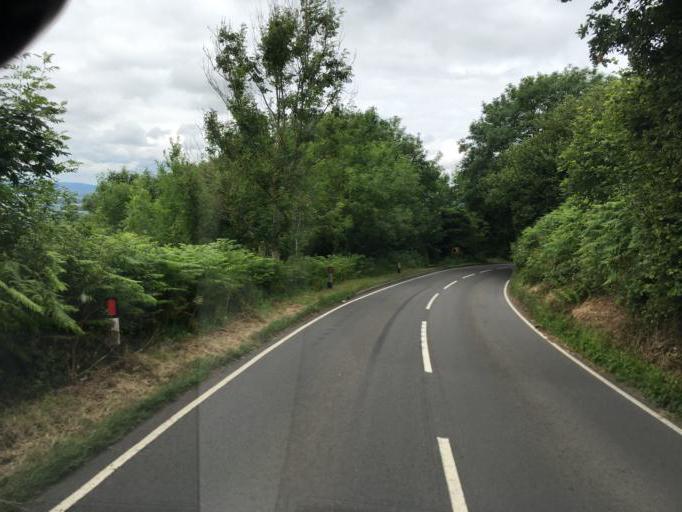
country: GB
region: England
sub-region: Gloucestershire
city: Stonehouse
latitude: 51.7075
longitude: -2.3022
